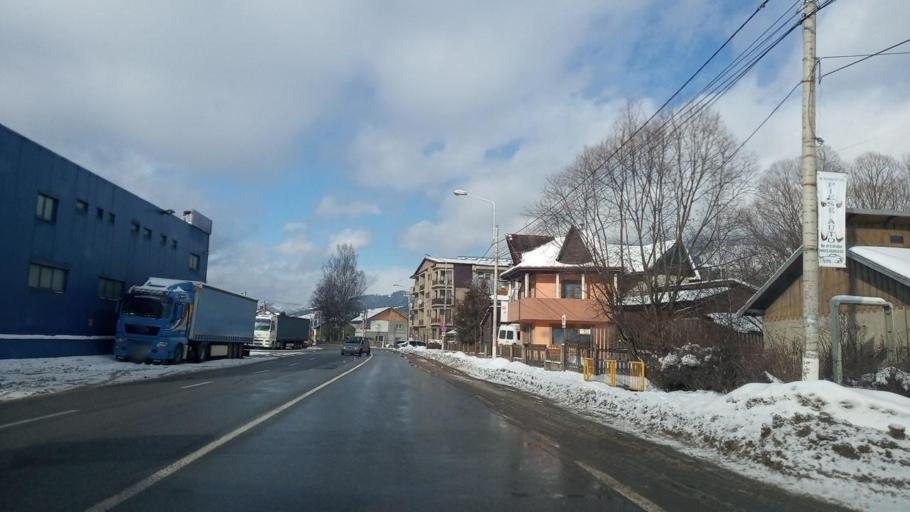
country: RO
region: Suceava
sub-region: Municipiul Vatra Dornei
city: Vatra Dornei
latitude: 47.3497
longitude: 25.3617
